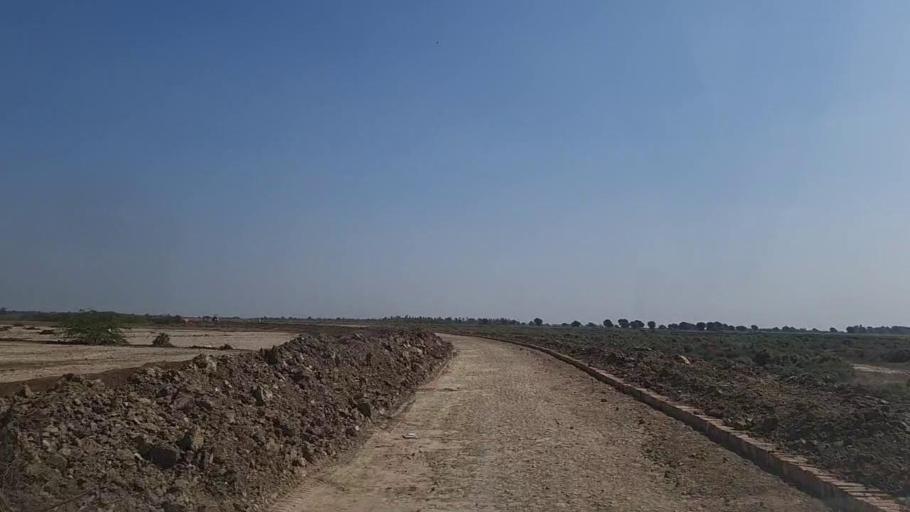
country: PK
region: Sindh
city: Digri
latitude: 25.1617
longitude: 69.1738
